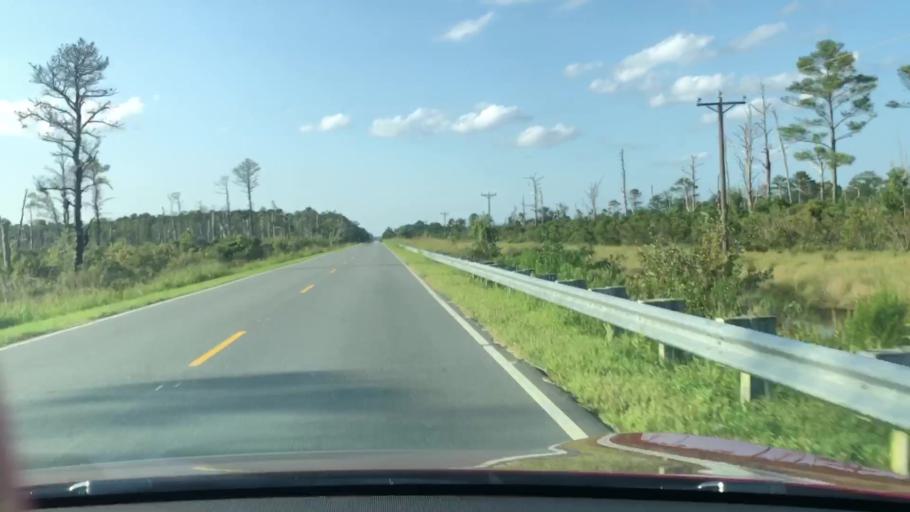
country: US
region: North Carolina
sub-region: Dare County
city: Wanchese
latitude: 35.6632
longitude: -75.7777
